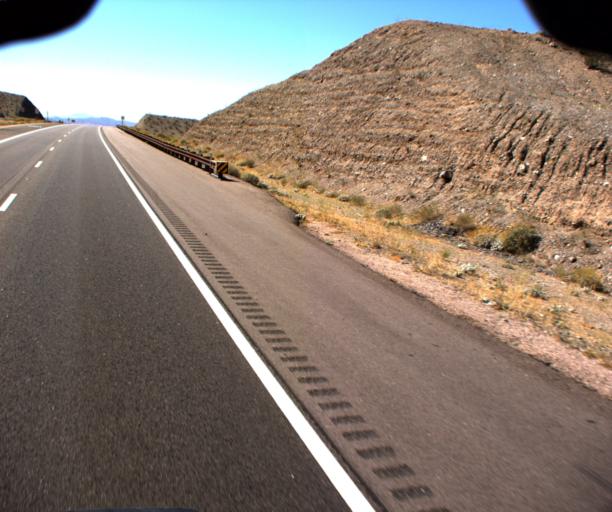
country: US
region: Nevada
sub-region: Clark County
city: Boulder City
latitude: 35.9173
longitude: -114.6304
